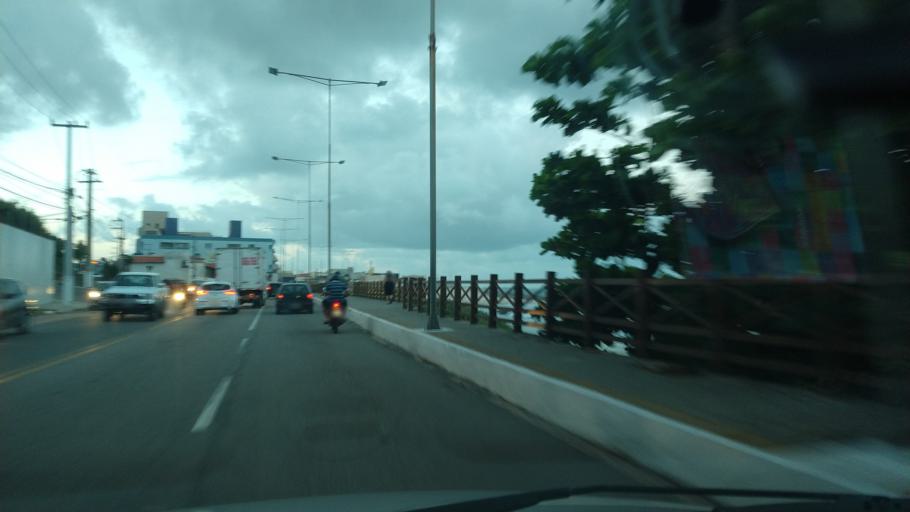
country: BR
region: Rio Grande do Norte
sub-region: Natal
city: Natal
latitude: -5.7874
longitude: -35.1895
